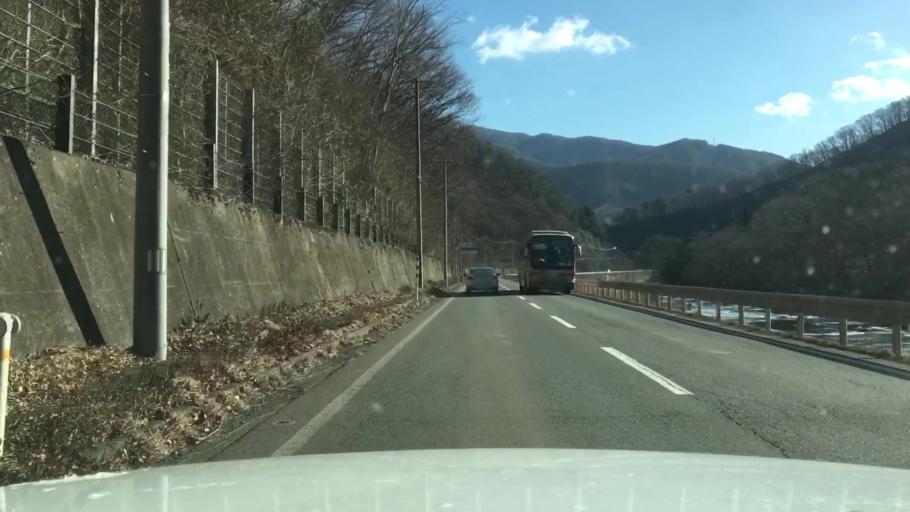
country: JP
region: Iwate
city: Tono
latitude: 39.6496
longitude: 141.5807
